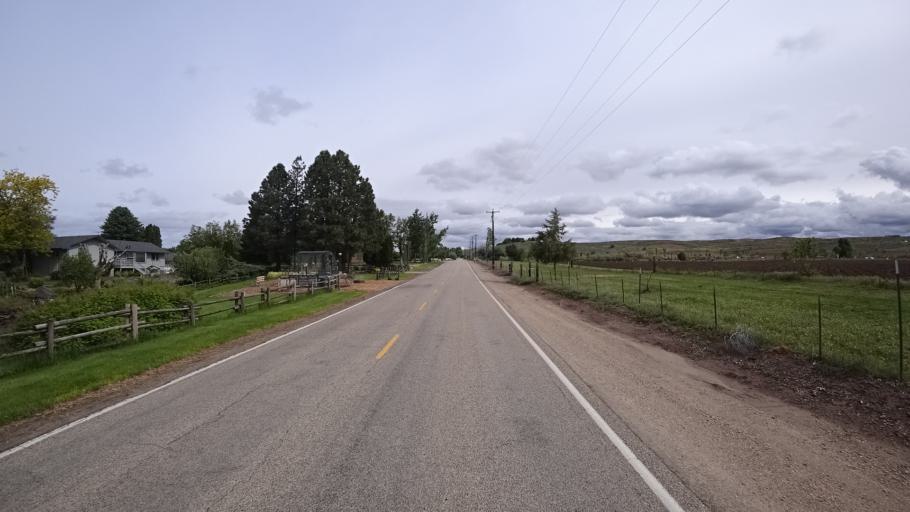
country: US
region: Idaho
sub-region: Ada County
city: Eagle
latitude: 43.7268
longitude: -116.3543
